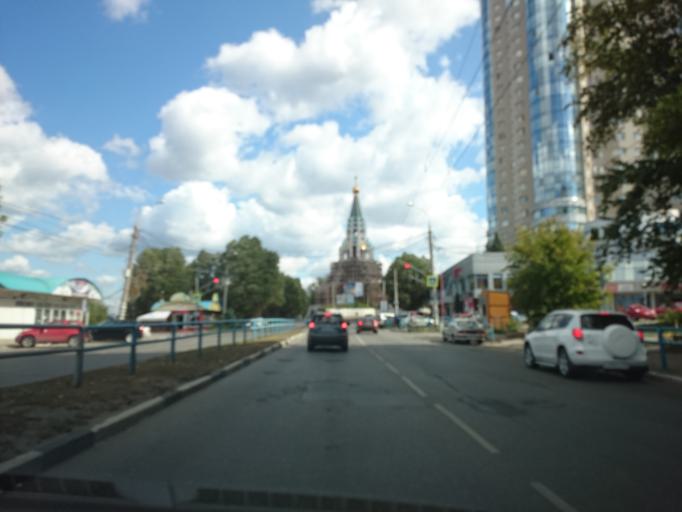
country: RU
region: Samara
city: Samara
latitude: 53.2152
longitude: 50.1321
